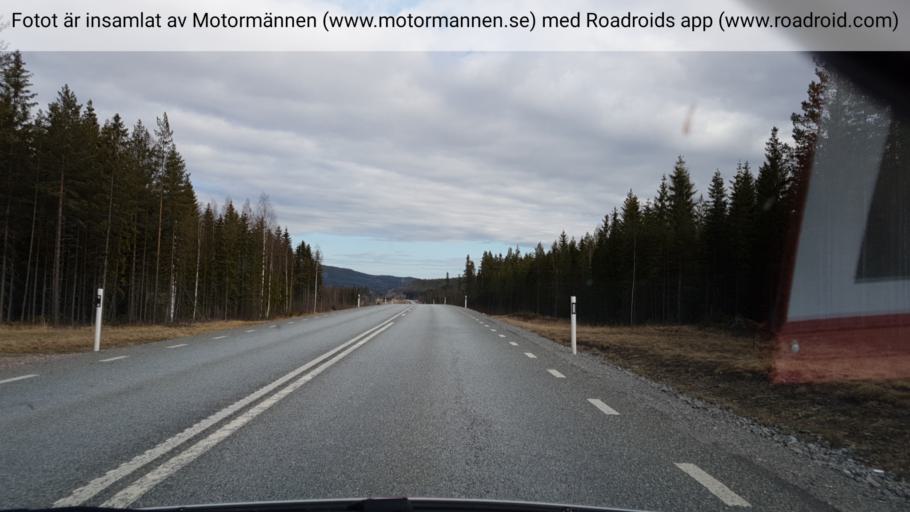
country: SE
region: Vaesternorrland
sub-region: Kramfors Kommun
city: Bollstabruk
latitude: 63.0451
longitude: 17.6317
